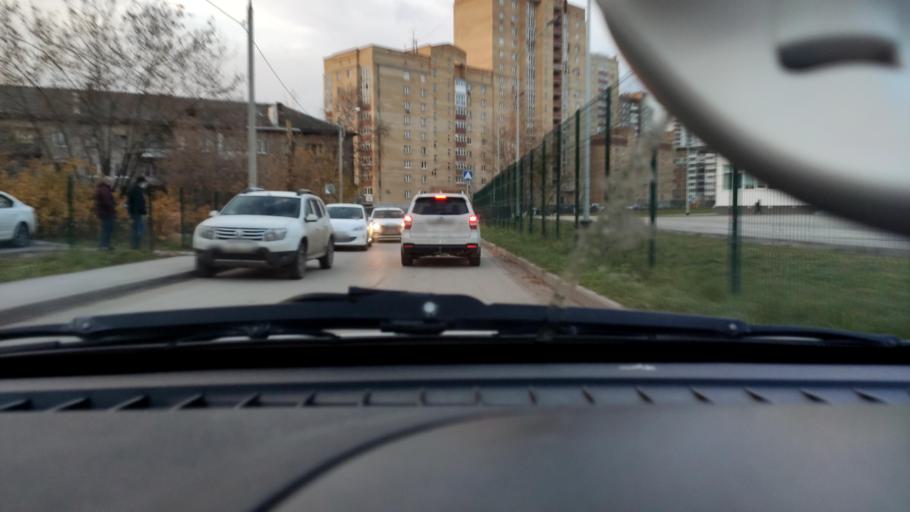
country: RU
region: Perm
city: Kondratovo
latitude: 57.9954
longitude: 56.1421
